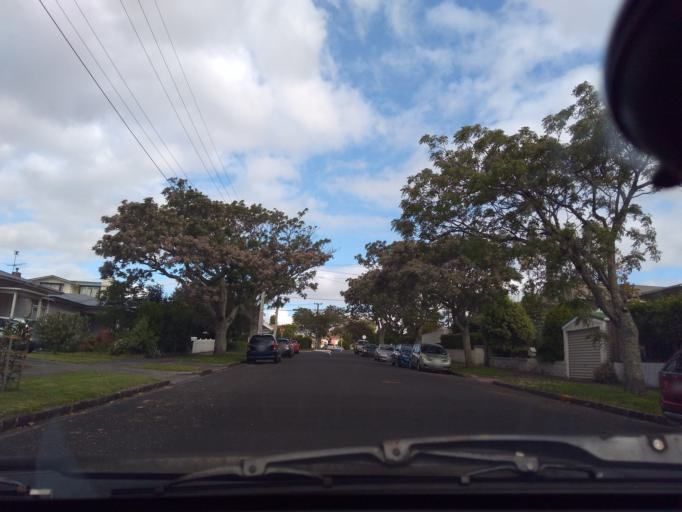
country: NZ
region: Auckland
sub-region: Auckland
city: Rosebank
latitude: -36.8763
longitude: 174.7179
